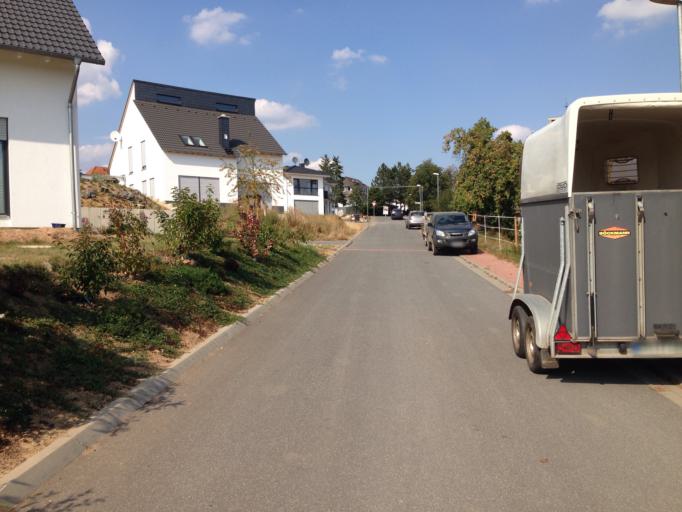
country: DE
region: Hesse
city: Lollar
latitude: 50.6294
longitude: 8.6730
